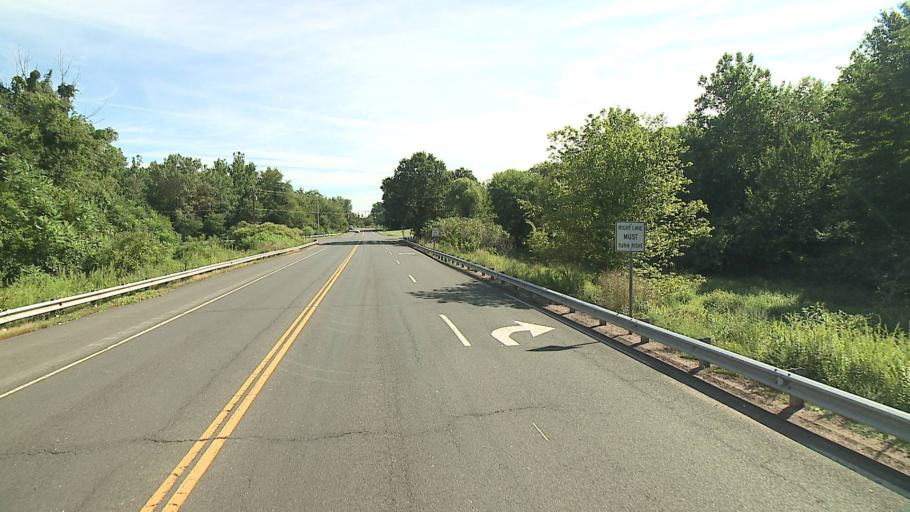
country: US
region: Connecticut
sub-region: Hartford County
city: Tariffville
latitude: 41.9164
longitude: -72.7407
